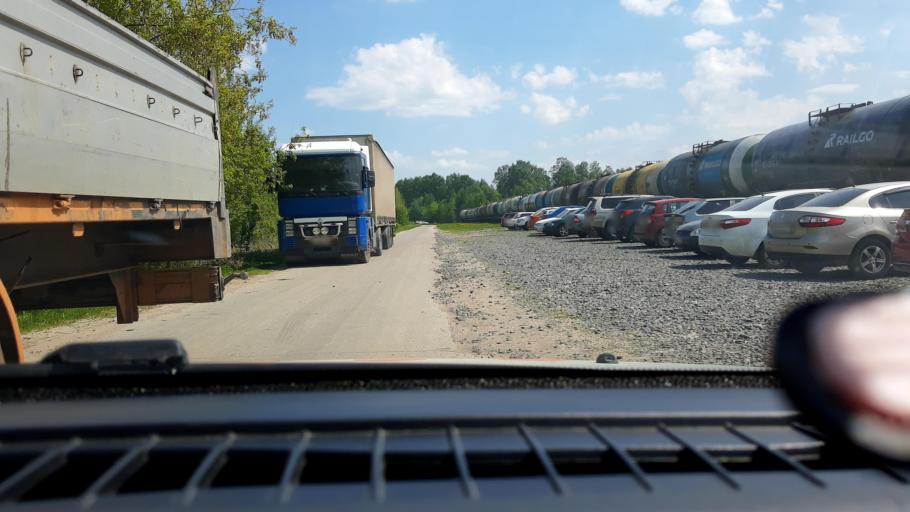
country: RU
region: Nizjnij Novgorod
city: Kstovo
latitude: 56.1467
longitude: 44.1172
